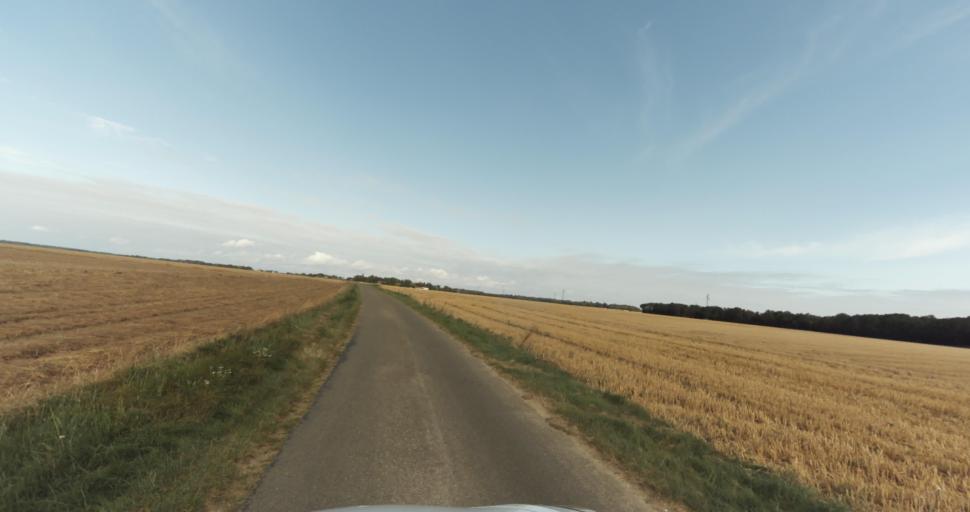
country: FR
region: Haute-Normandie
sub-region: Departement de l'Eure
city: Nonancourt
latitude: 48.8226
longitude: 1.1583
